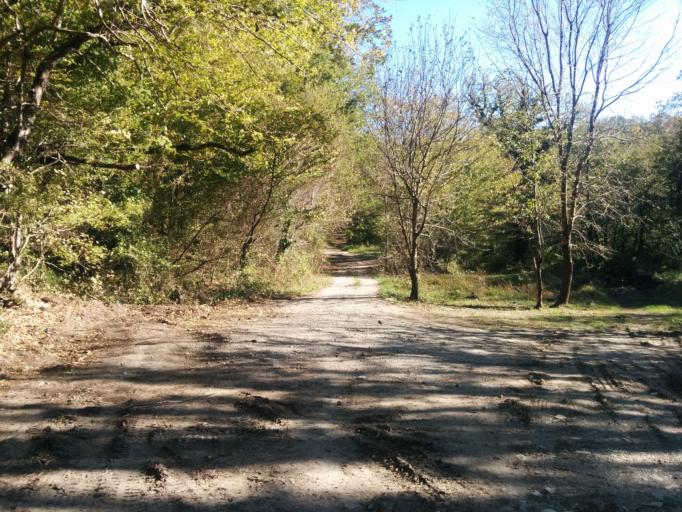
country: RU
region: Krasnodarskiy
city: Agoy
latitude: 44.1505
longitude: 39.0161
